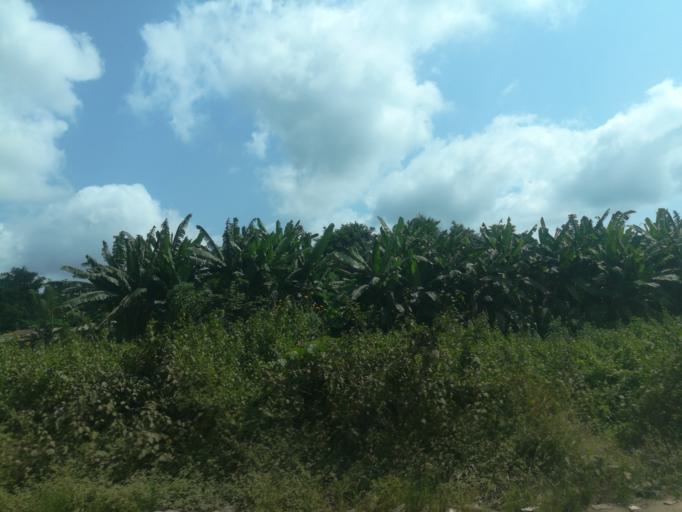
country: NG
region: Oyo
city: Moniya
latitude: 7.5907
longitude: 3.9127
